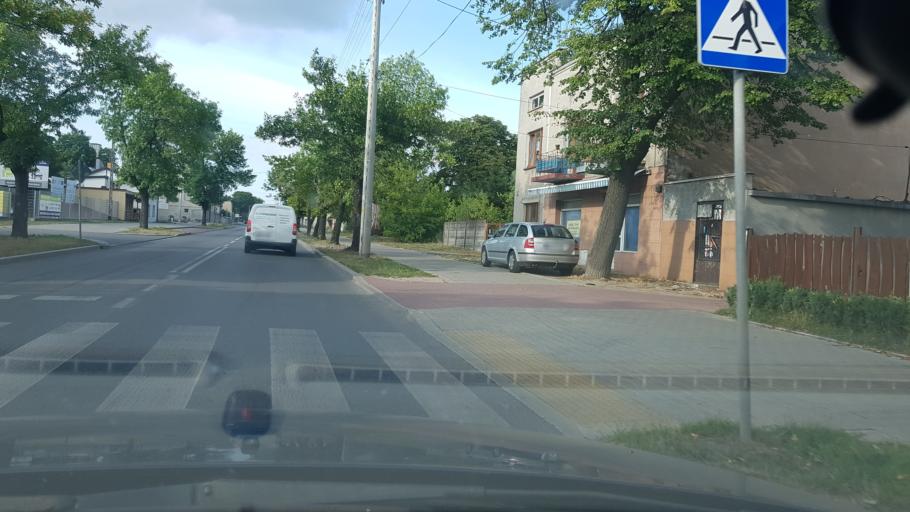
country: PL
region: Lodz Voivodeship
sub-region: Powiat tomaszowski
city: Tomaszow Mazowiecki
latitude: 51.5508
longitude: 20.0164
